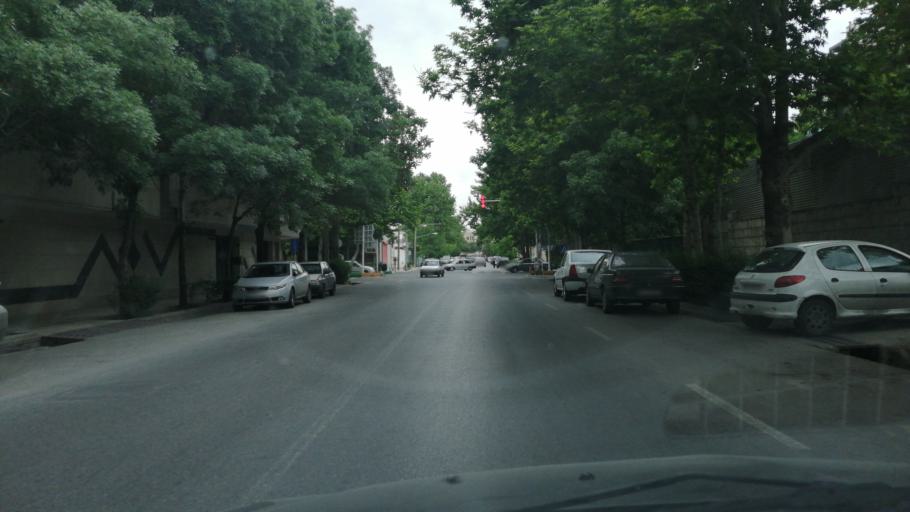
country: IR
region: Razavi Khorasan
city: Mashhad
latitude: 36.2852
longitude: 59.5710
